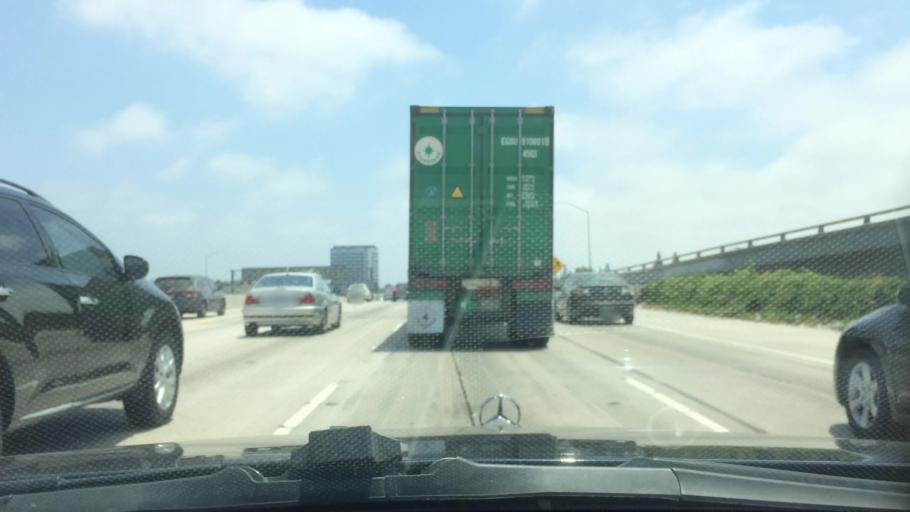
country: US
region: California
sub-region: Los Angeles County
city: Culver City
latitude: 34.0235
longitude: -118.4230
